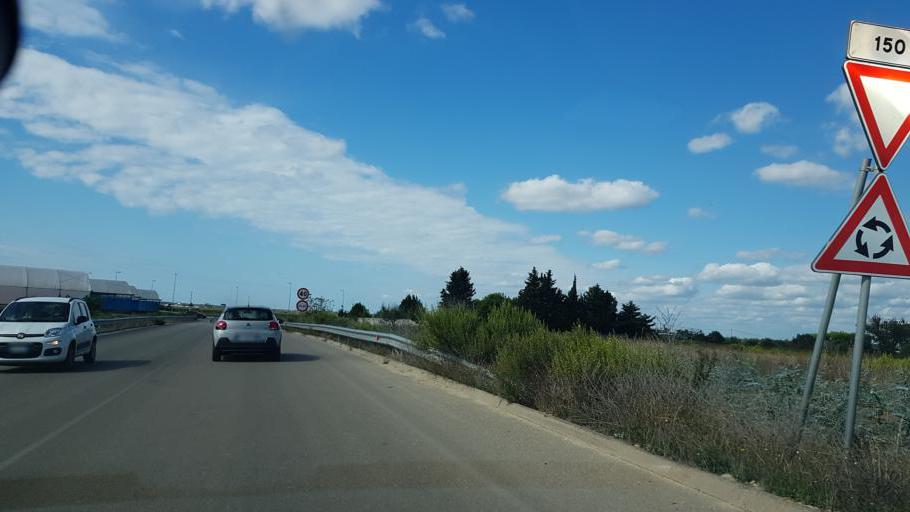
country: IT
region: Apulia
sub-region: Provincia di Lecce
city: Leverano
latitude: 40.3061
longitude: 17.9920
